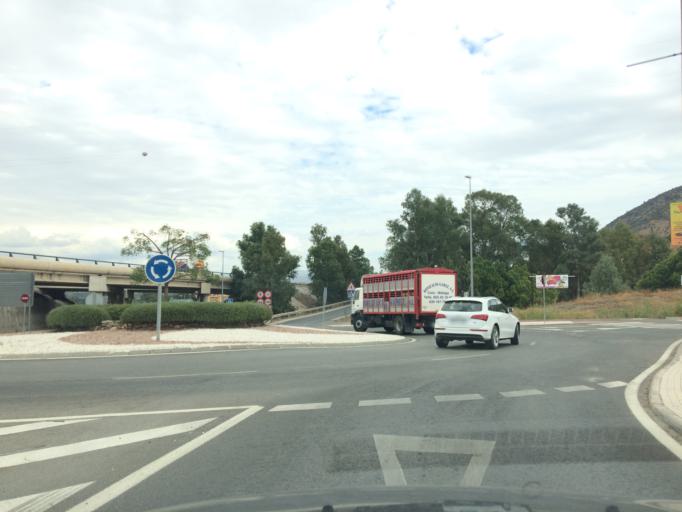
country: ES
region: Andalusia
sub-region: Provincia de Malaga
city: Cartama
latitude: 36.7171
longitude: -4.6226
